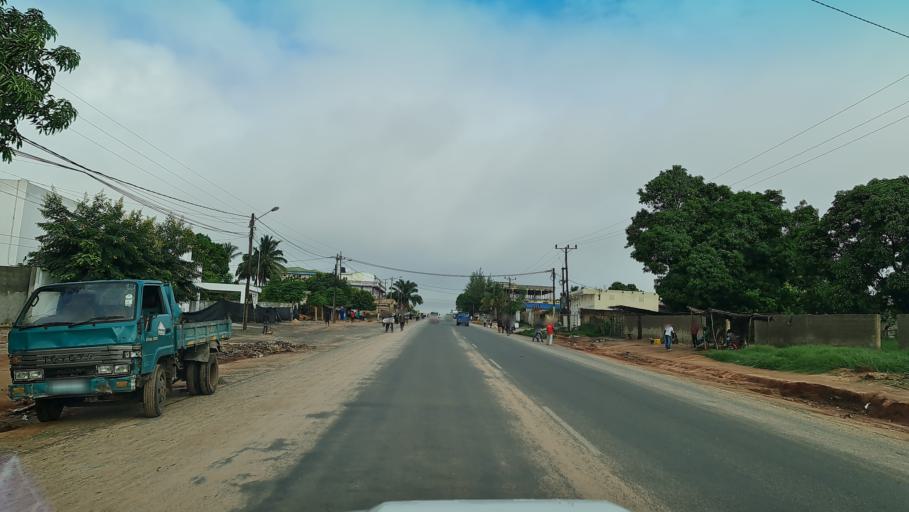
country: MZ
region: Nampula
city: Nampula
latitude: -15.1379
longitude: 39.2843
